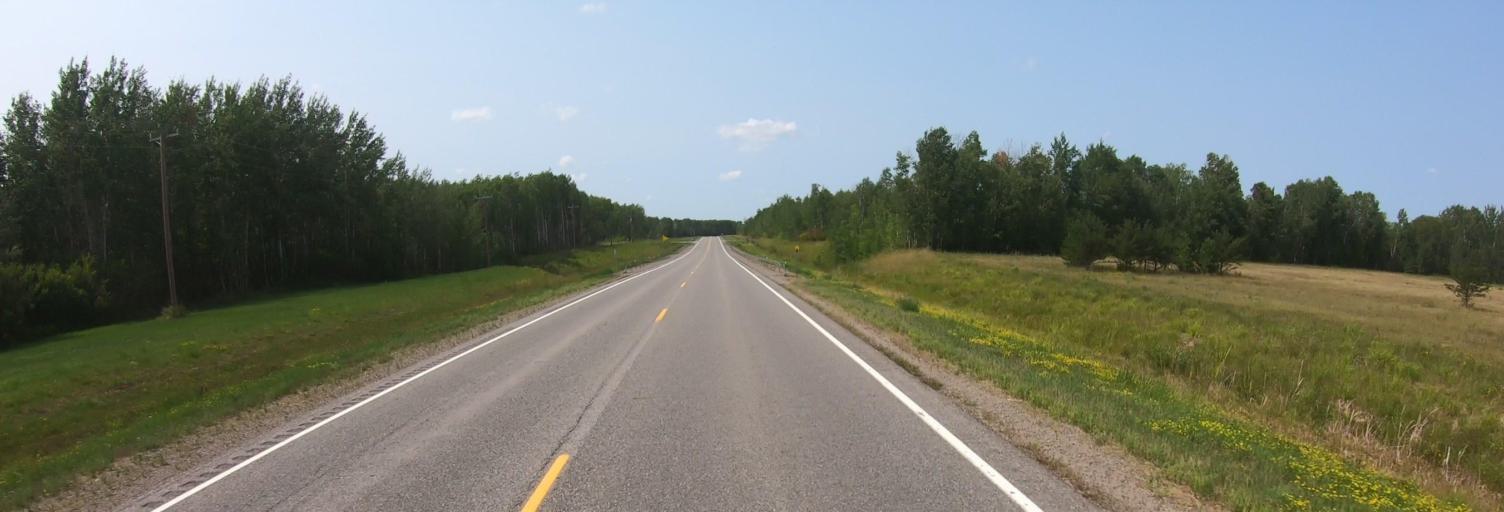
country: US
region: Minnesota
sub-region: Lake of the Woods County
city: Baudette
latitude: 48.6476
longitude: -94.2309
